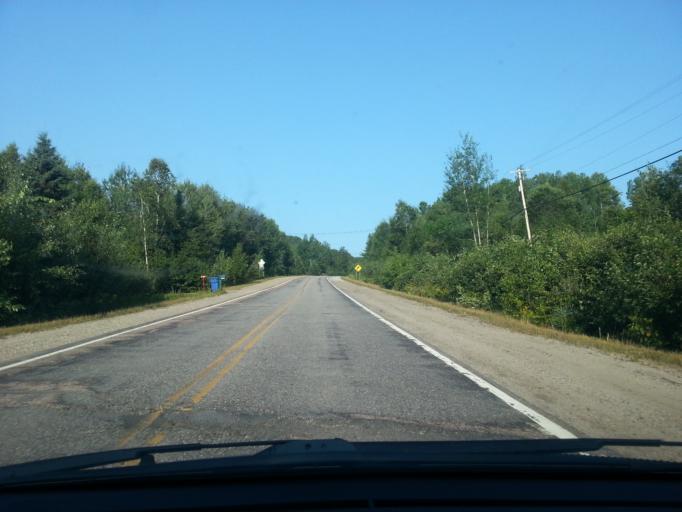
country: CA
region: Quebec
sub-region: Outaouais
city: Maniwaki
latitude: 46.1054
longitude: -76.1090
